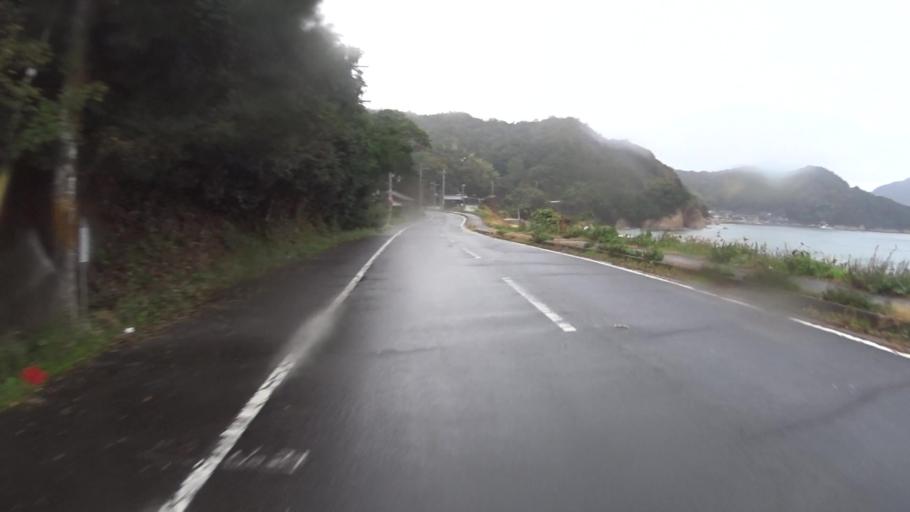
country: JP
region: Kyoto
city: Miyazu
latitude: 35.5687
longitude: 135.2525
